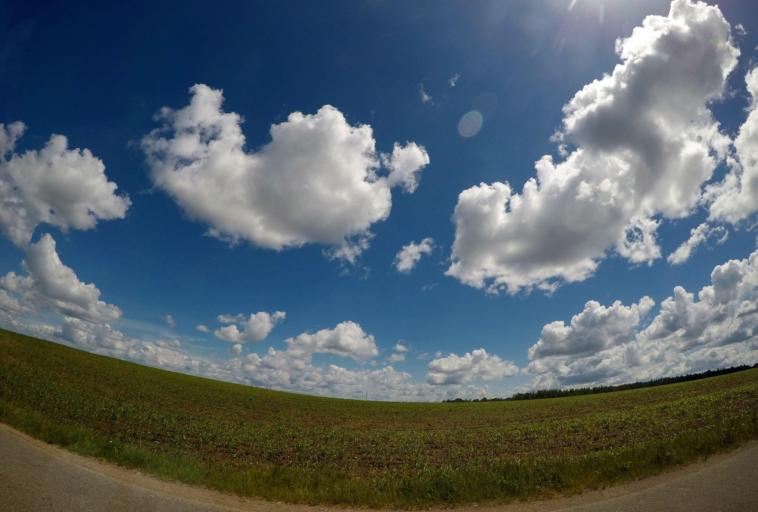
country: BY
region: Grodnenskaya
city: Hal'shany
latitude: 54.1704
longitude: 26.0988
